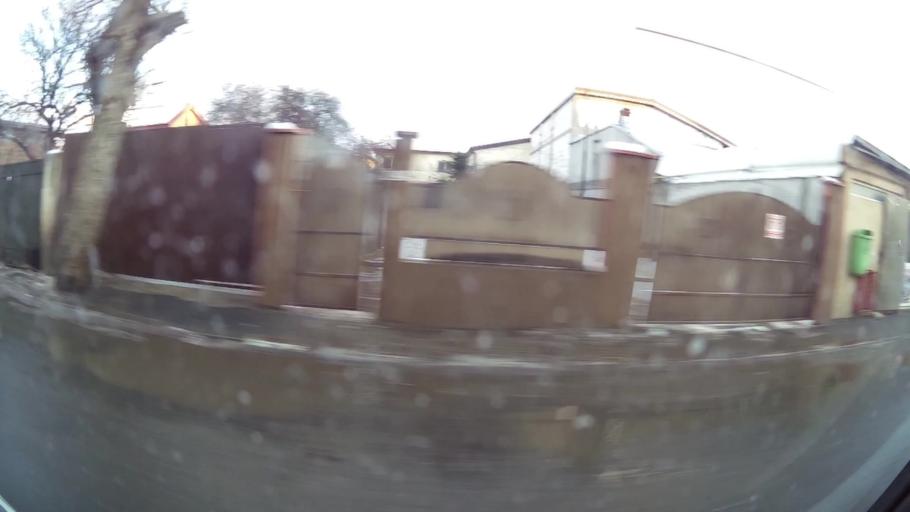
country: RO
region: Ilfov
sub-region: Comuna Popesti-Leordeni
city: Popesti-Leordeni
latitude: 44.3781
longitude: 26.1471
